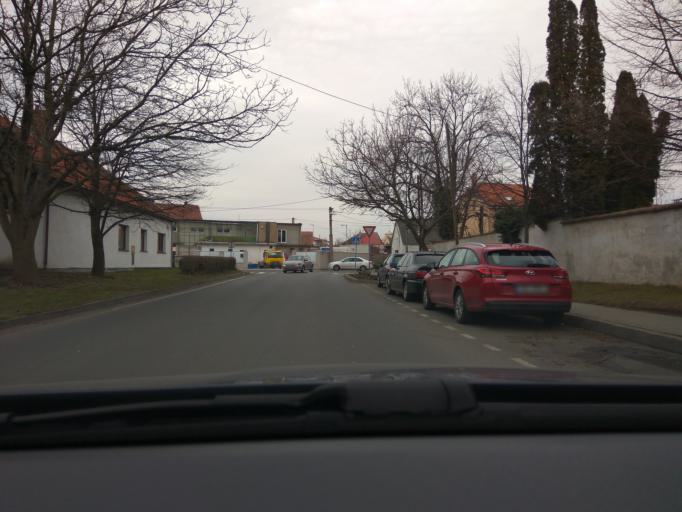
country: CZ
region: Central Bohemia
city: Libeznice
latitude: 50.1913
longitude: 14.4949
